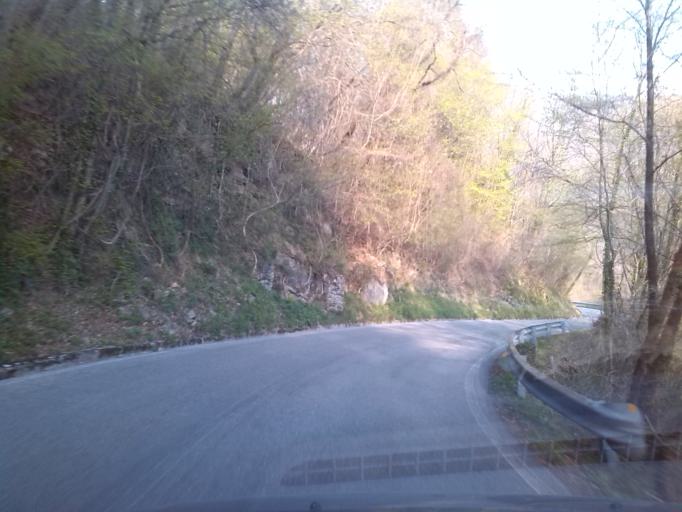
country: IT
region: Friuli Venezia Giulia
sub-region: Provincia di Udine
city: Savogna
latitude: 46.1728
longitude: 13.5595
